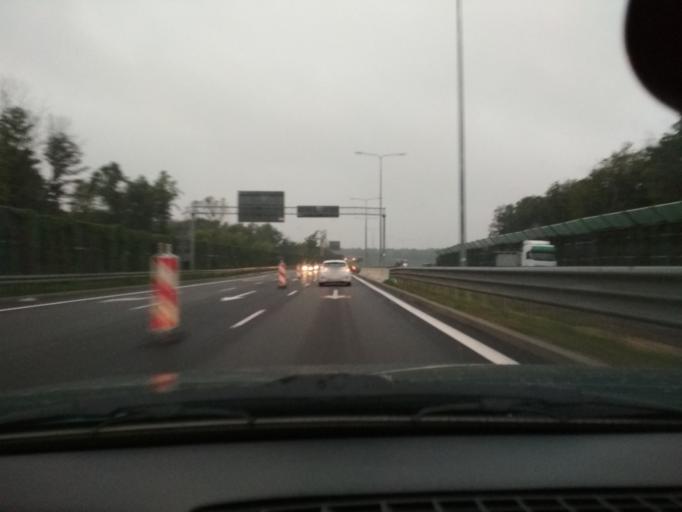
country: PL
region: Silesian Voivodeship
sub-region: Zabrze
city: Zabrze
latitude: 50.2884
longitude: 18.7803
